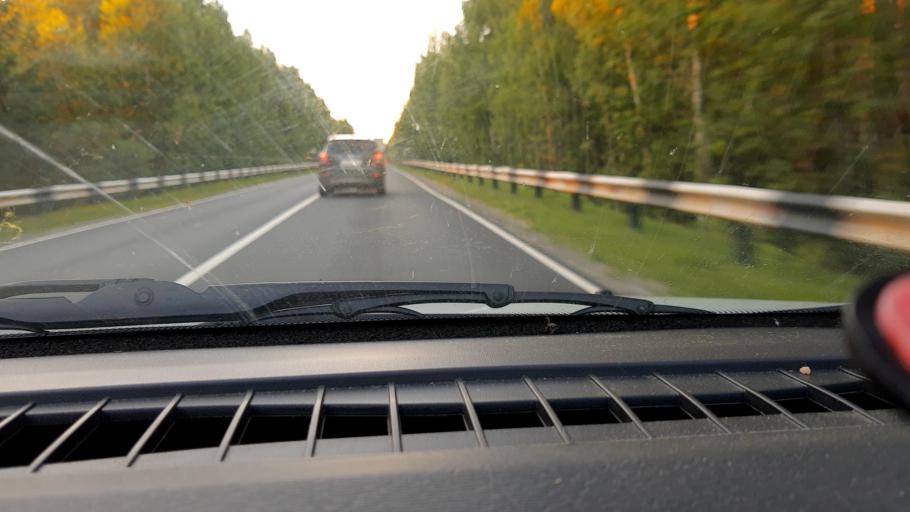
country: RU
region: Nizjnij Novgorod
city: Krasnyye Baki
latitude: 57.1223
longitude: 45.2107
